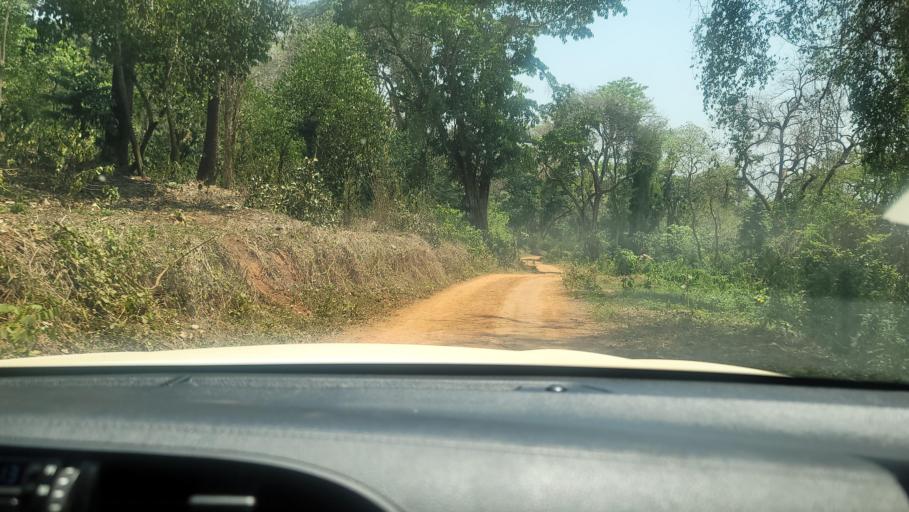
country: ET
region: Southern Nations, Nationalities, and People's Region
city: Bonga
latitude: 7.5085
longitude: 36.2291
